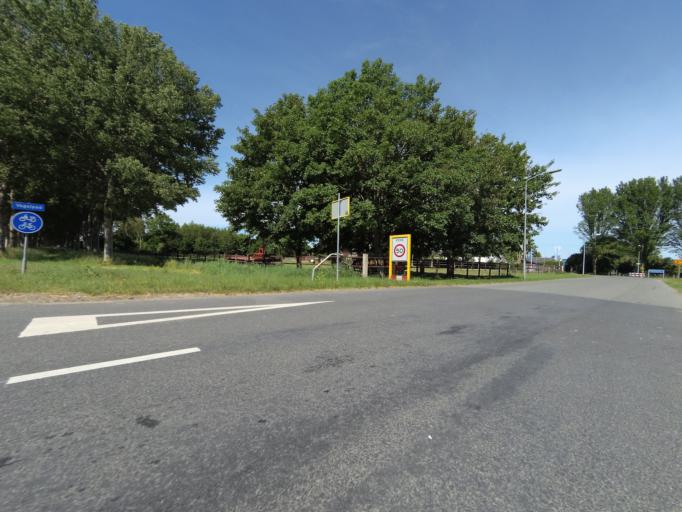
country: NL
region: North Holland
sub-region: Gemeente Huizen
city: Huizen
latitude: 52.3452
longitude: 5.3255
